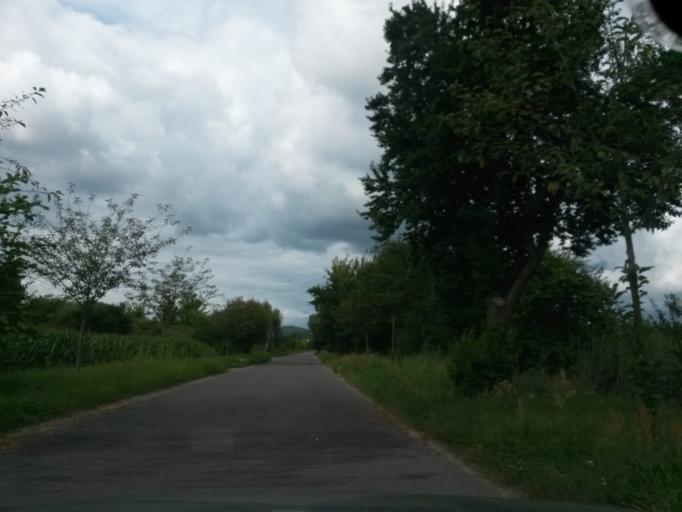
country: DE
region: Brandenburg
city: Oderberg
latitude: 52.8629
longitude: 14.0632
